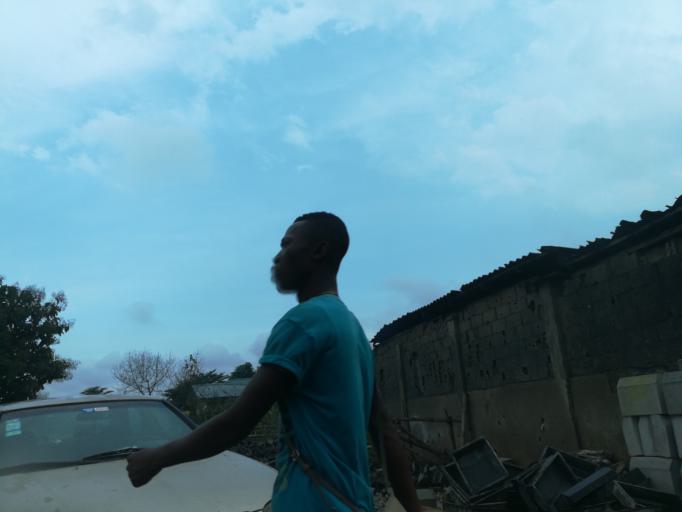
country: NG
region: Lagos
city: Oshodi
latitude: 6.5777
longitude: 3.3409
